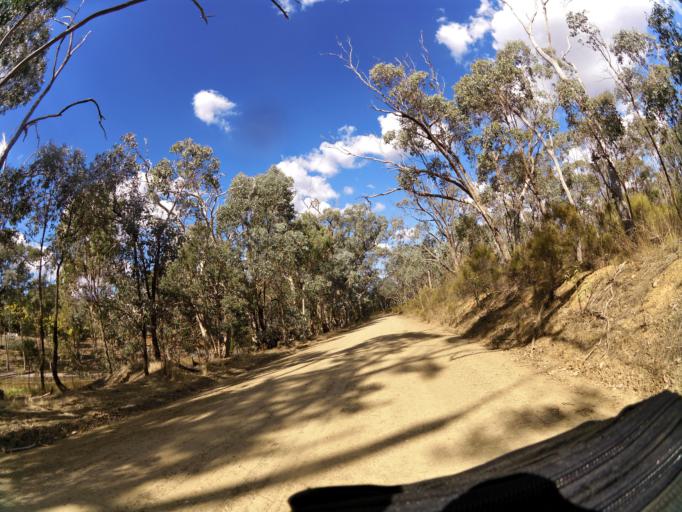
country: AU
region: Victoria
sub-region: Greater Bendigo
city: Kennington
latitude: -36.9592
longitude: 144.7748
